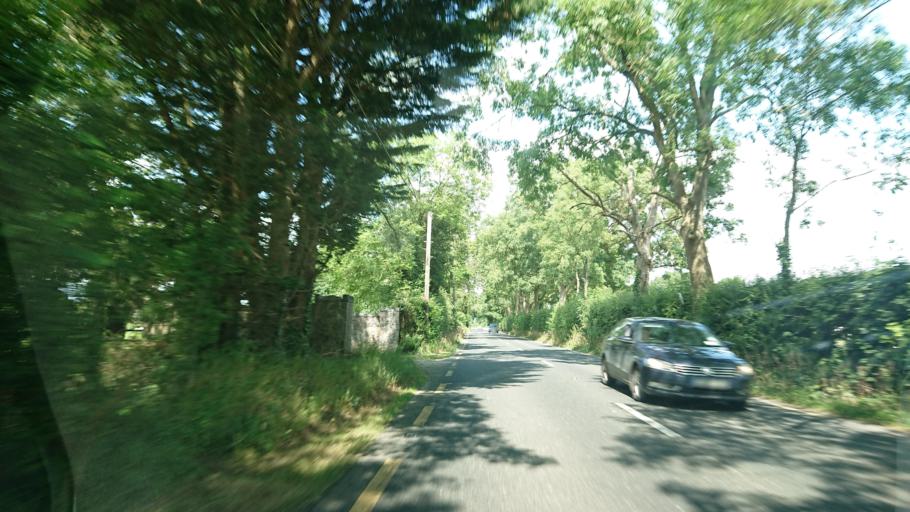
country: IE
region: Leinster
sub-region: Kildare
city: Kilcock
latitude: 53.3574
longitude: -6.6955
